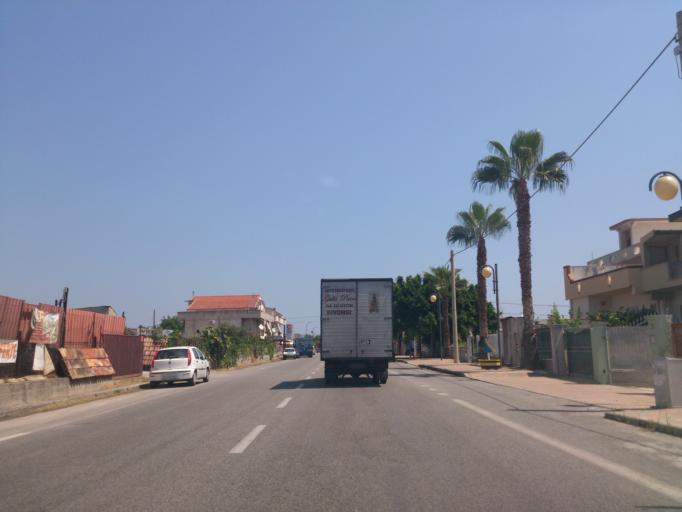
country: IT
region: Calabria
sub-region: Provincia di Reggio Calabria
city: Riace Marina
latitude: 38.3902
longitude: 16.5299
